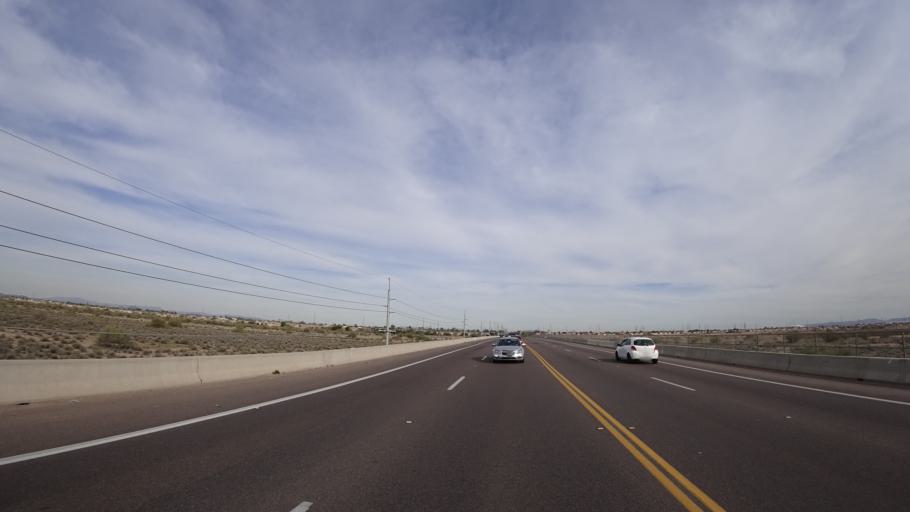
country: US
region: Arizona
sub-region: Maricopa County
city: Youngtown
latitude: 33.5654
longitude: -112.3172
